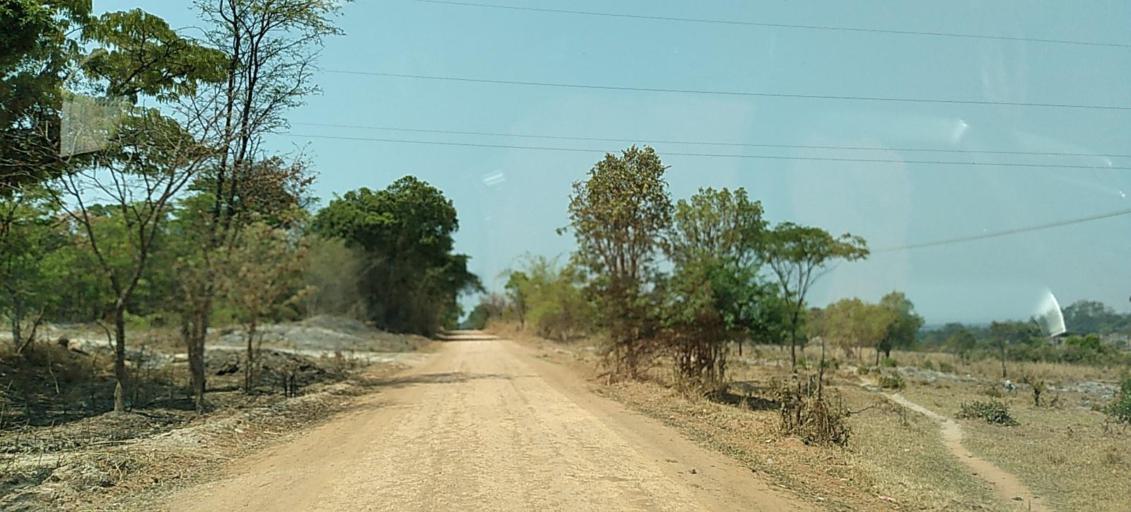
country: ZM
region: Copperbelt
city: Chambishi
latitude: -12.6132
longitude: 27.9576
